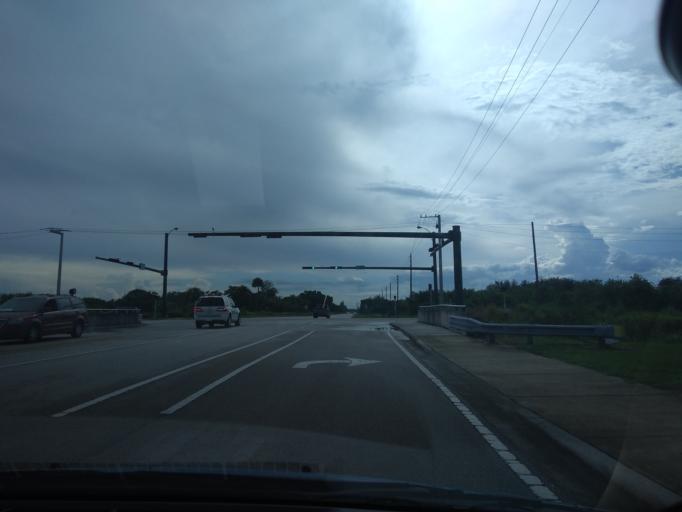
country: US
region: Florida
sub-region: Indian River County
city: West Vero Corridor
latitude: 27.6318
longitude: -80.4627
